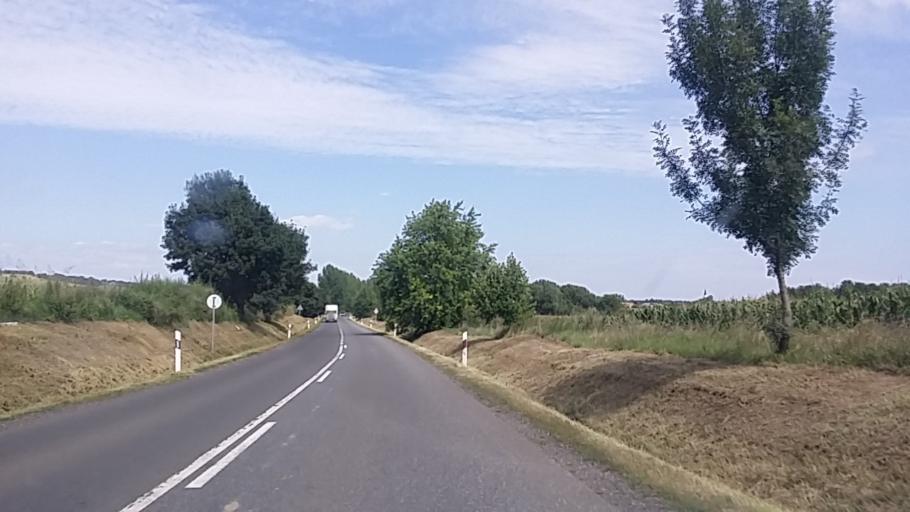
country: HU
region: Tolna
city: Dombovar
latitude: 46.3191
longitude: 18.1319
